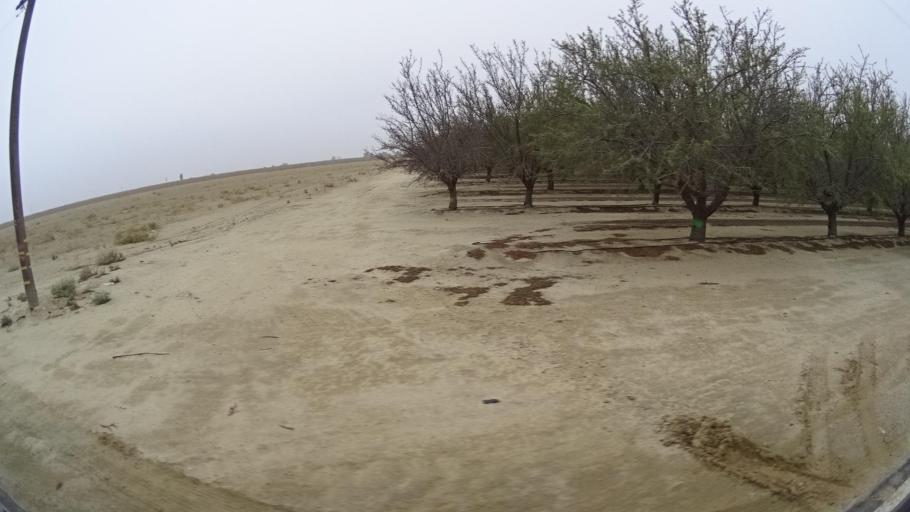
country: US
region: California
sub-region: Kern County
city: Lost Hills
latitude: 35.6122
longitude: -119.5803
